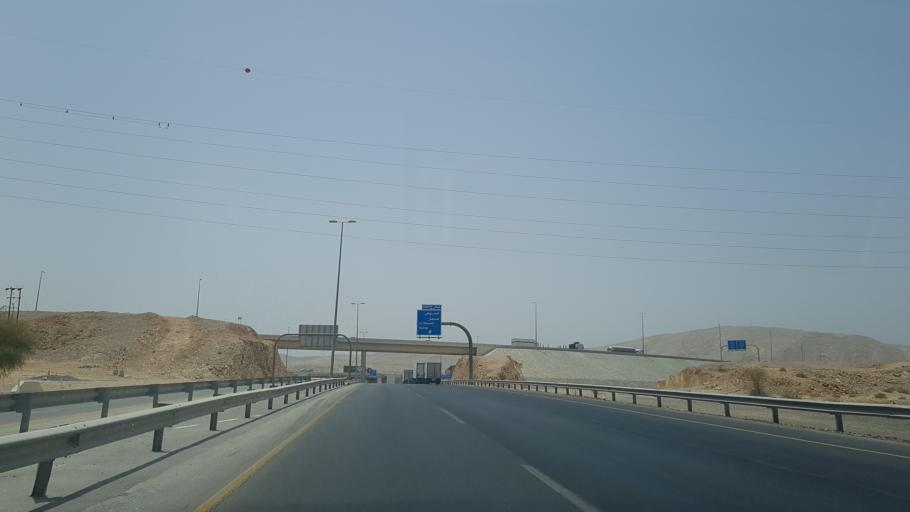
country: OM
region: Muhafazat Masqat
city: As Sib al Jadidah
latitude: 23.5704
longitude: 58.1909
